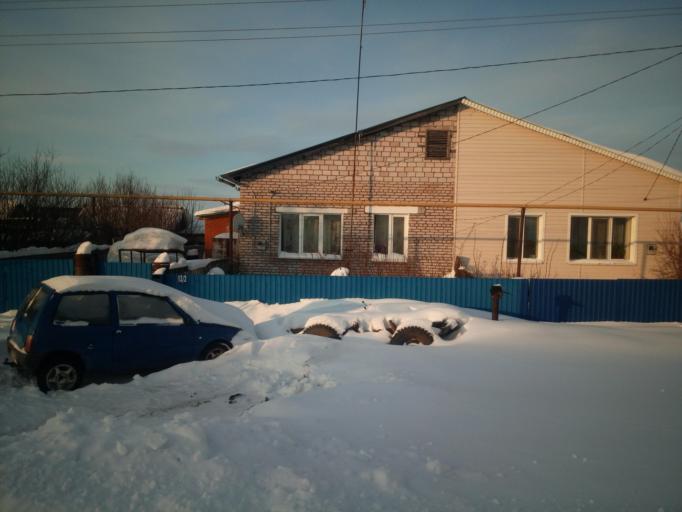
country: RU
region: Bashkortostan
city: Amzya
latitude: 56.1650
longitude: 54.3789
